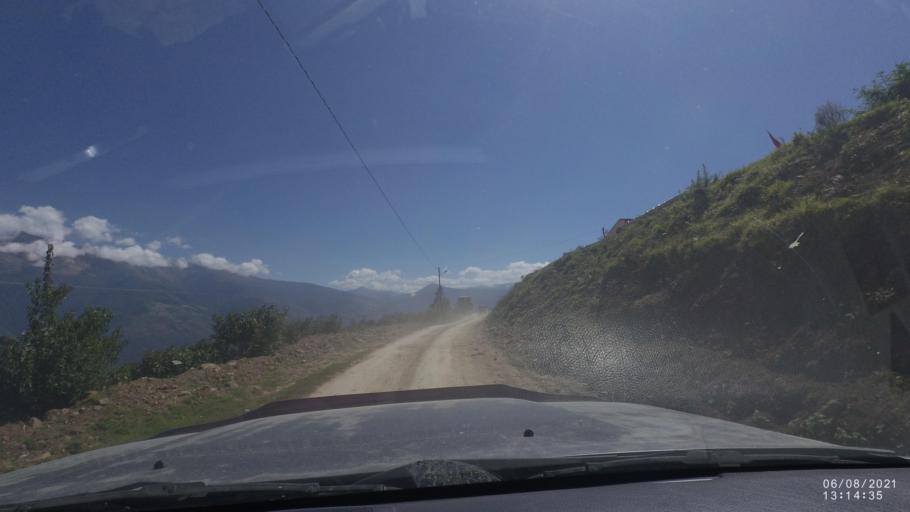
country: BO
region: La Paz
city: Quime
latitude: -16.7077
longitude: -66.7126
